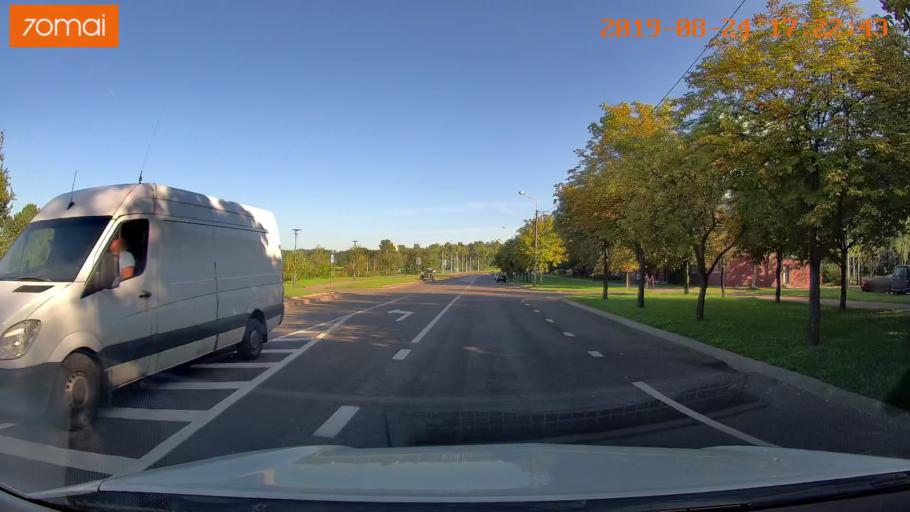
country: BY
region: Minsk
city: Hatava
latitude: 53.8445
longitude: 27.6471
